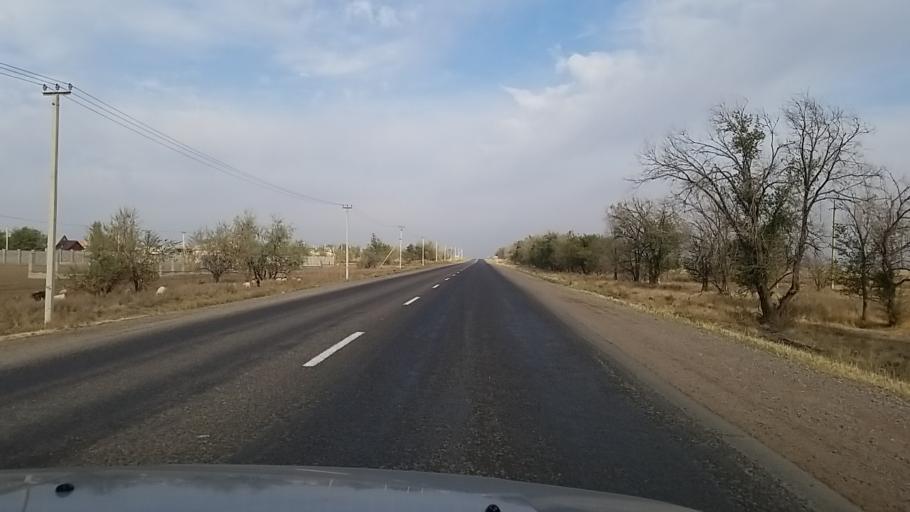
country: KZ
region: Almaty Oblysy
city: Burunday
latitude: 43.4820
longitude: 76.6760
